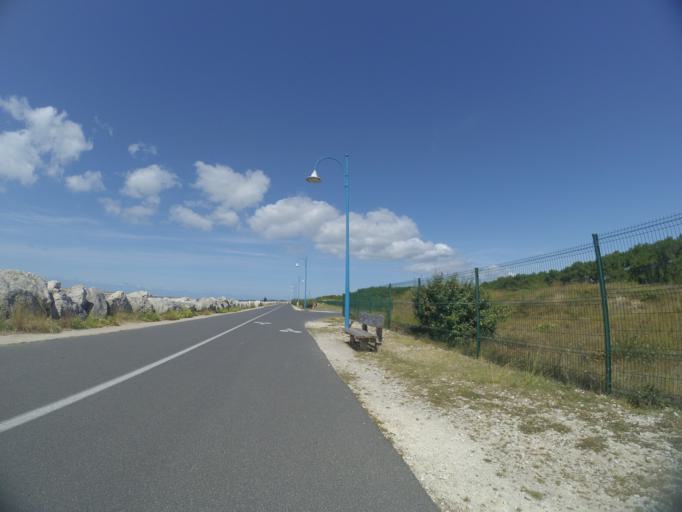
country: FR
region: Poitou-Charentes
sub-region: Departement de la Charente-Maritime
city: Les Mathes
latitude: 45.6763
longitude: -1.1681
